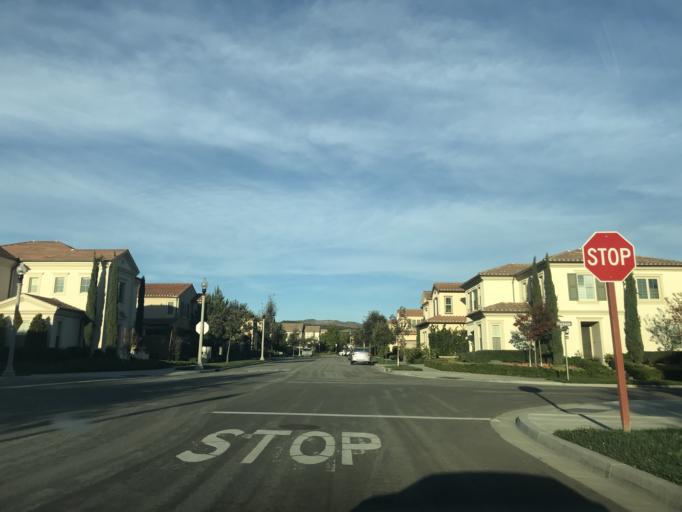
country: US
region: California
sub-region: Orange County
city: North Tustin
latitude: 33.7098
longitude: -117.7449
